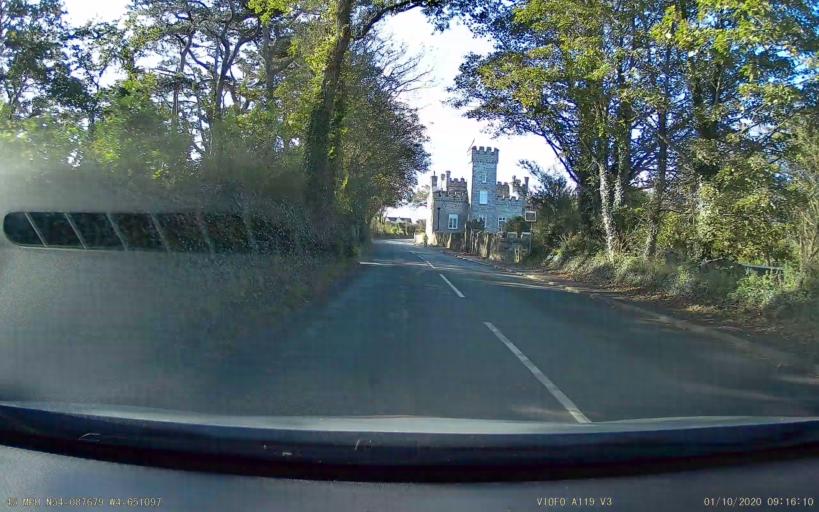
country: IM
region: Castletown
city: Castletown
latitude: 54.0879
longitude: -4.6511
